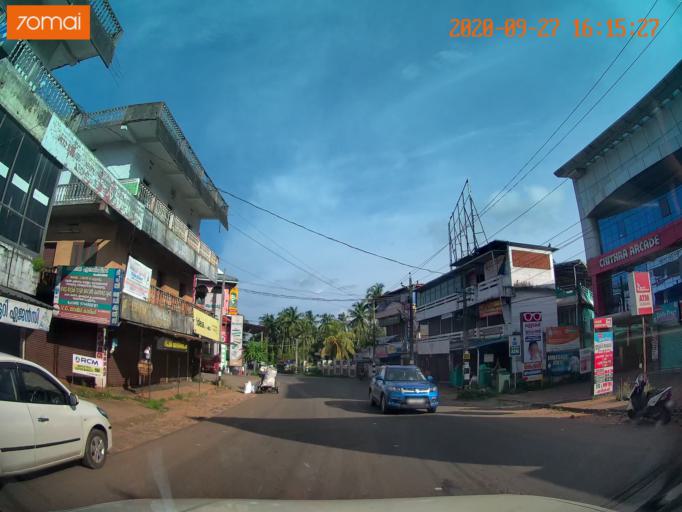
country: IN
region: Kerala
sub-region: Thrissur District
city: Trichur
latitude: 10.4544
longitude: 76.2539
